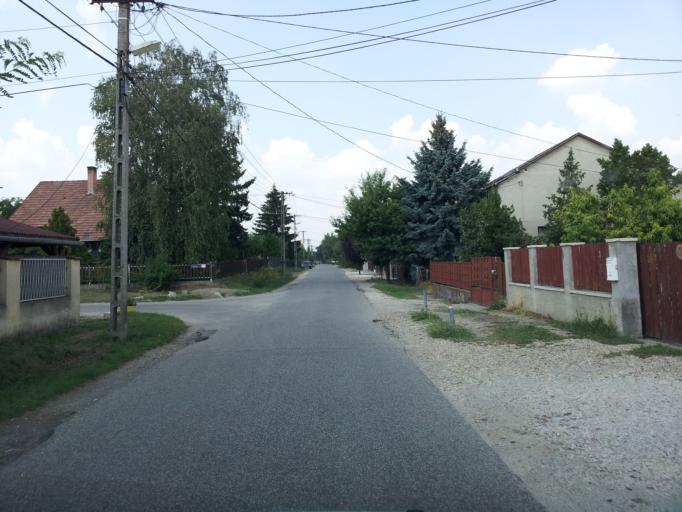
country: HU
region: Pest
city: Szigethalom
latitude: 47.3189
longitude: 19.0163
